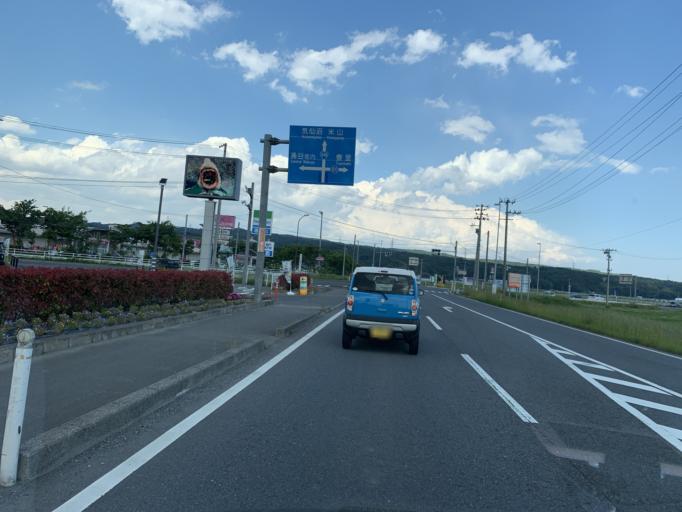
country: JP
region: Miyagi
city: Wakuya
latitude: 38.5350
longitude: 141.1468
